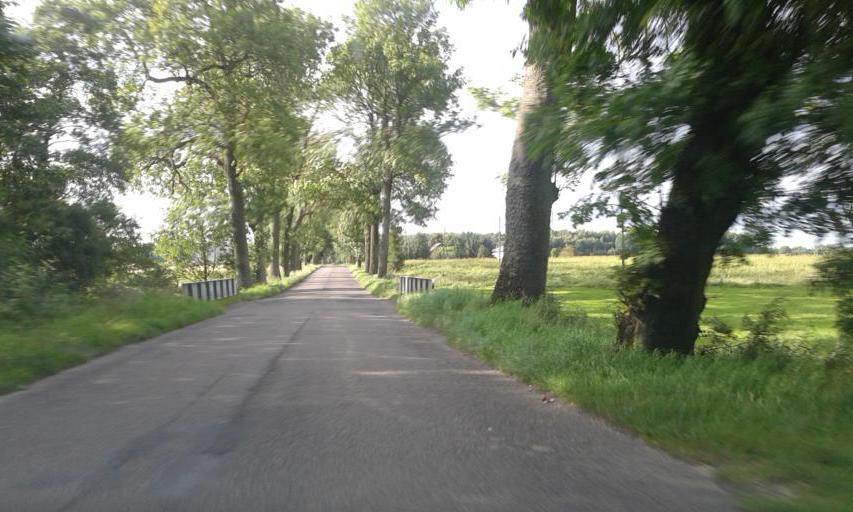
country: PL
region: West Pomeranian Voivodeship
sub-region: Powiat bialogardzki
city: Tychowo
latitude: 53.9110
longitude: 16.2417
